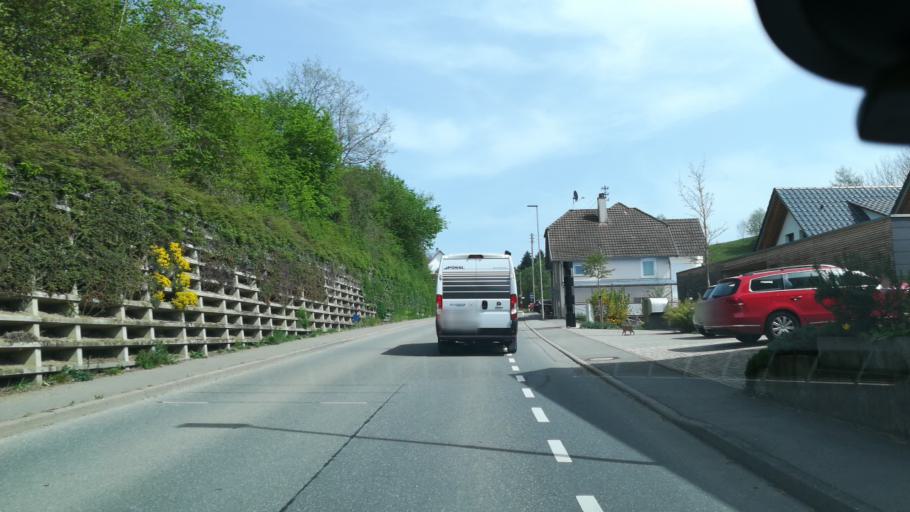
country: DE
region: Baden-Wuerttemberg
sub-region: Freiburg Region
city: Radolfzell am Bodensee
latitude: 47.7741
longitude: 8.9982
